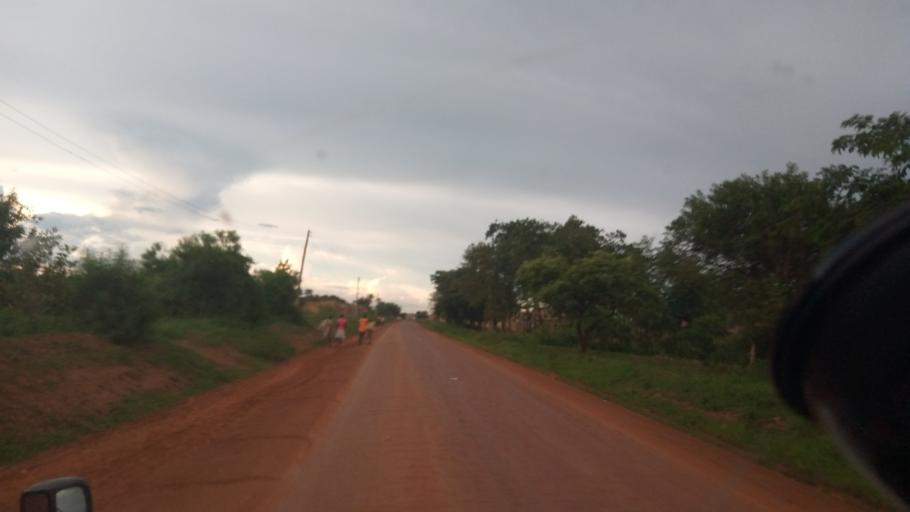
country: UG
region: Northern Region
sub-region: Kole District
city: Kole
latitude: 2.4783
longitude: 32.9359
